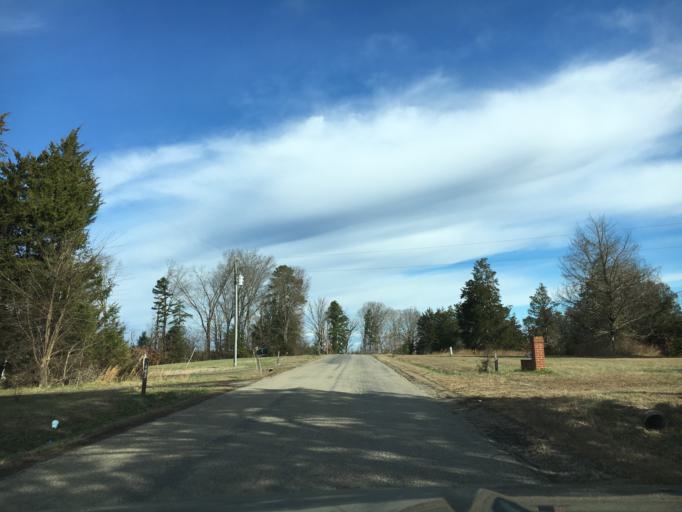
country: US
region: Virginia
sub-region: Nottoway County
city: Crewe
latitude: 37.2660
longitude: -78.2209
